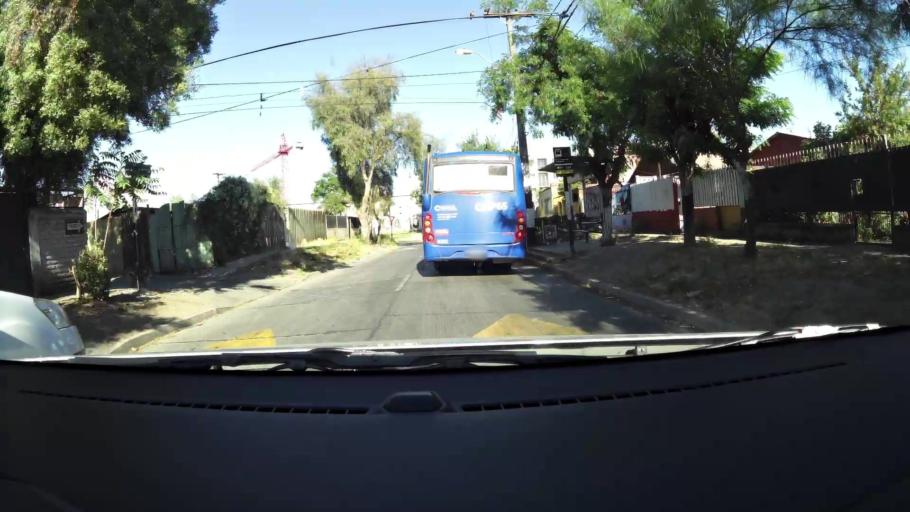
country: CL
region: Santiago Metropolitan
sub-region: Provincia de Maipo
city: San Bernardo
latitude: -33.5466
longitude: -70.6858
